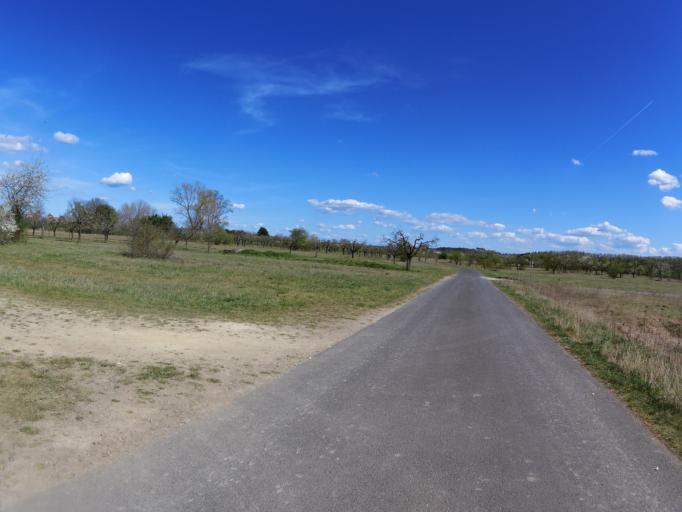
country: DE
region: Bavaria
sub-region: Regierungsbezirk Unterfranken
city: Nordheim
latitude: 49.8588
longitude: 10.2066
